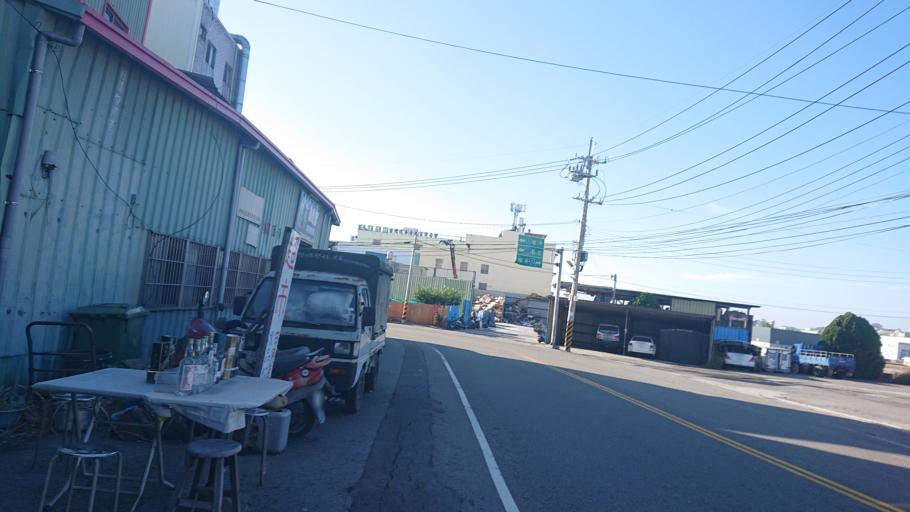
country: TW
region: Taiwan
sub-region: Changhua
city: Chang-hua
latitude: 24.1191
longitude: 120.5770
